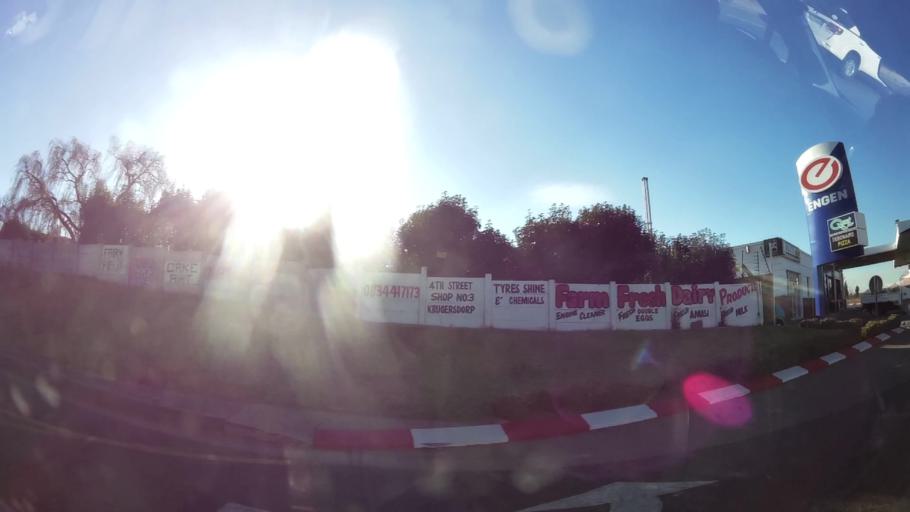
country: ZA
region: Gauteng
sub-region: West Rand District Municipality
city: Krugersdorp
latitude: -26.0997
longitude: 27.7800
